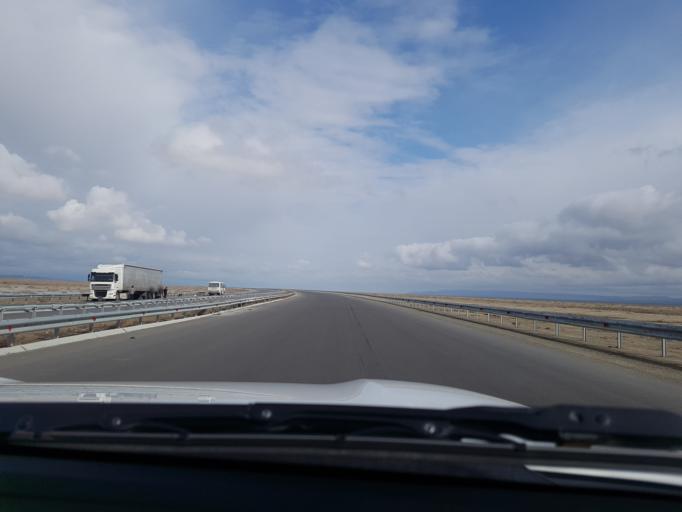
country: TM
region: Balkan
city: Gumdag
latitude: 39.1794
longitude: 54.9596
